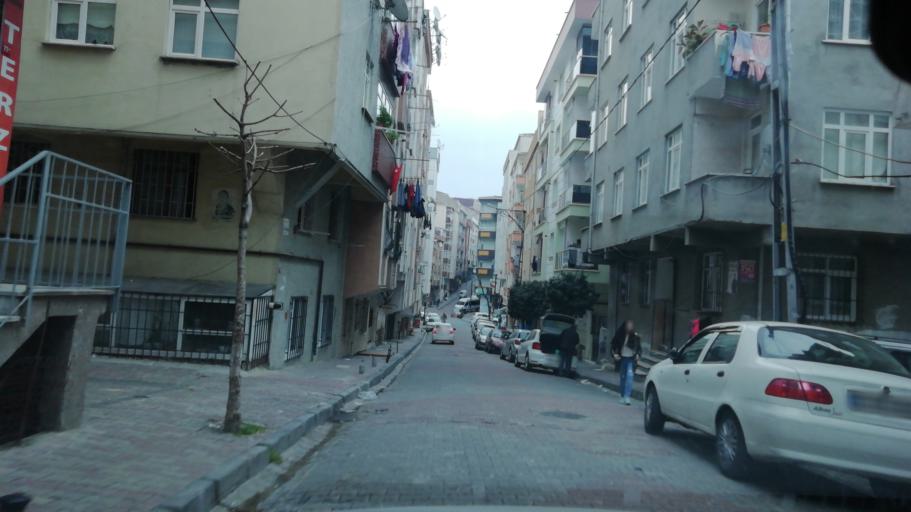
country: TR
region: Istanbul
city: Bahcelievler
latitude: 41.0067
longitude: 28.8375
